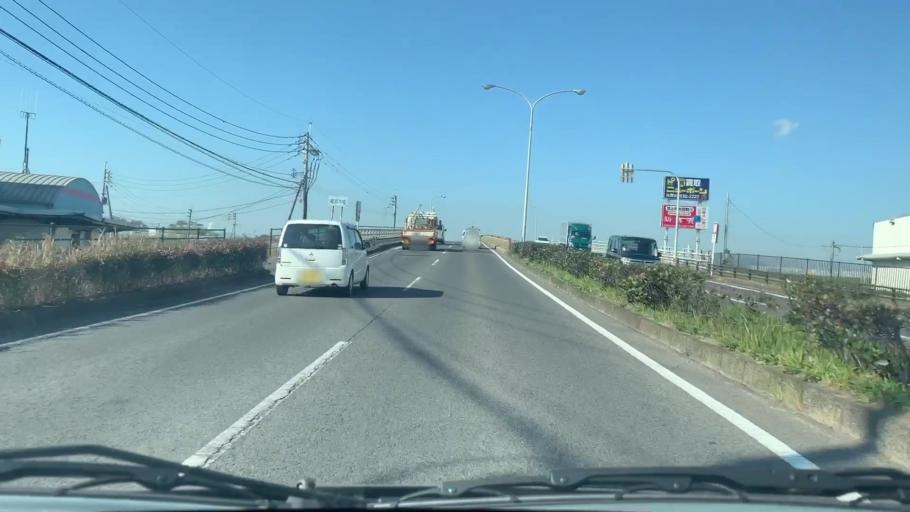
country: JP
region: Saga Prefecture
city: Saga-shi
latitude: 33.2652
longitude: 130.2469
